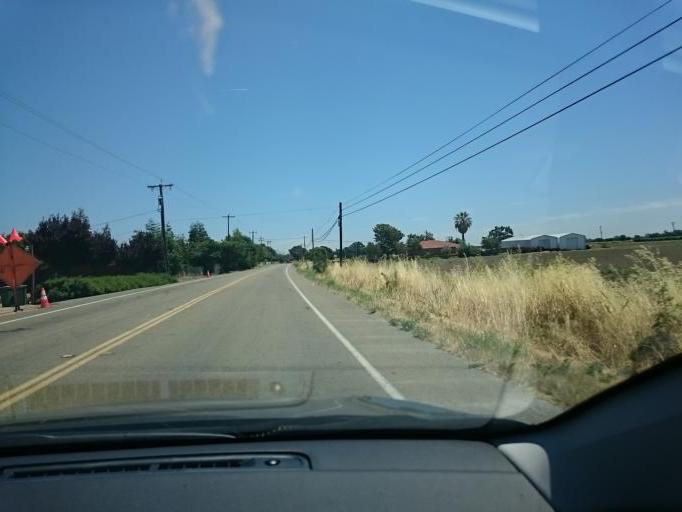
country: US
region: California
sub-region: San Joaquin County
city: Thornton
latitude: 38.2261
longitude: -121.4418
